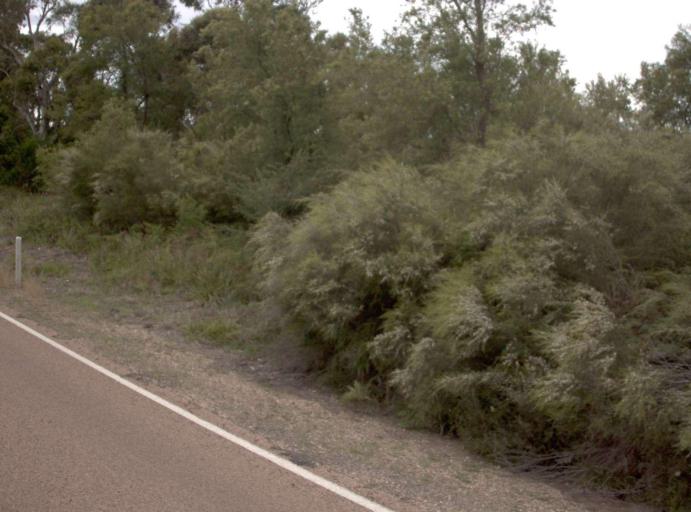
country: AU
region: Victoria
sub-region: East Gippsland
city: Bairnsdale
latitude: -37.9836
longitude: 147.4047
